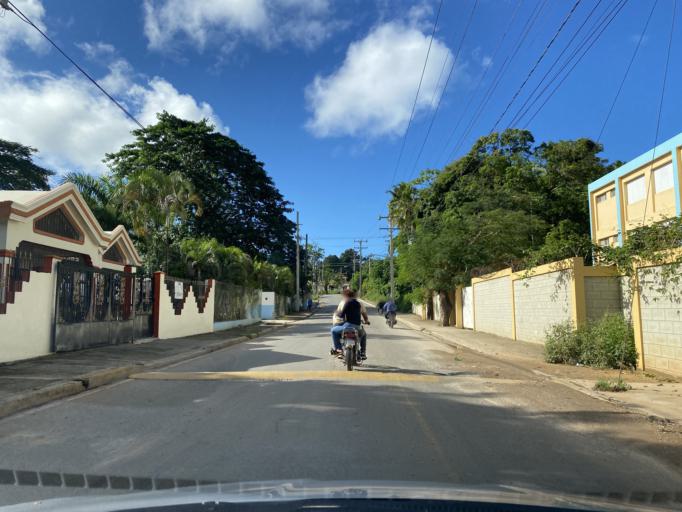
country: DO
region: Samana
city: Las Terrenas
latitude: 19.2945
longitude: -69.5486
